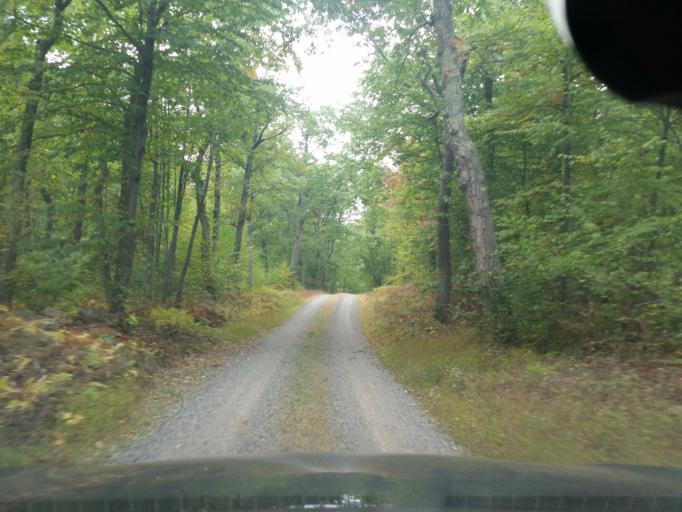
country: US
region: Pennsylvania
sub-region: Lycoming County
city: Jersey Shore
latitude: 41.0843
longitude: -77.1816
